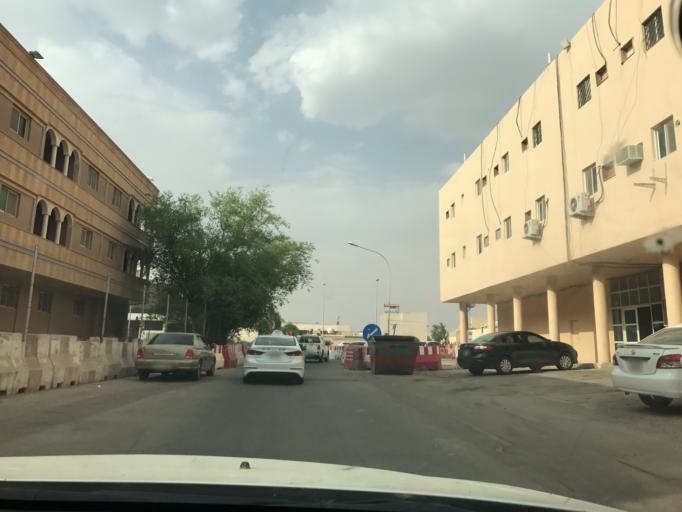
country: SA
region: Ar Riyad
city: Riyadh
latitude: 24.7077
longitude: 46.7113
